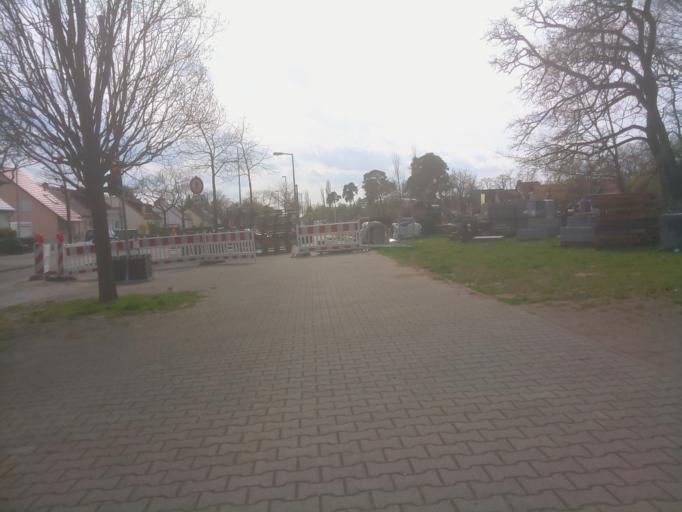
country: DE
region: Baden-Wuerttemberg
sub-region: Karlsruhe Region
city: Mannheim
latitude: 49.5367
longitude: 8.4955
